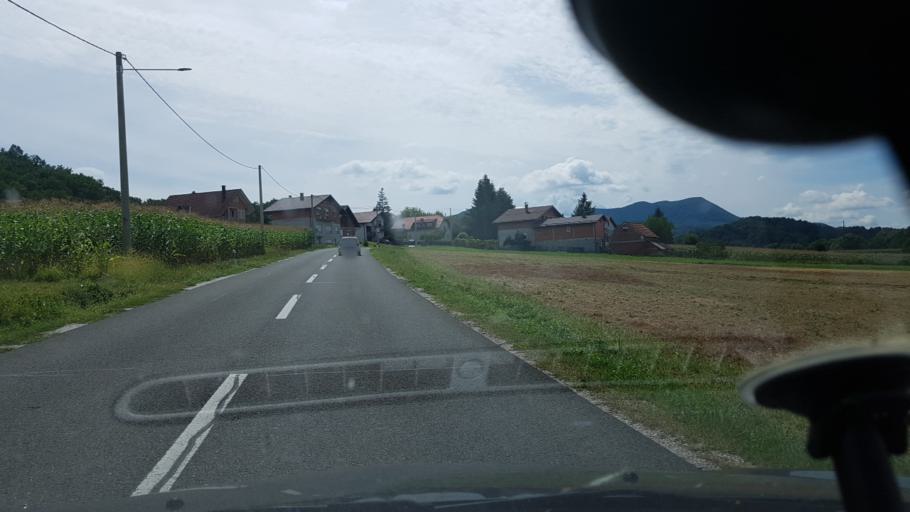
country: HR
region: Varazdinska
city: Lepoglava
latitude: 46.2245
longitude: 15.9775
